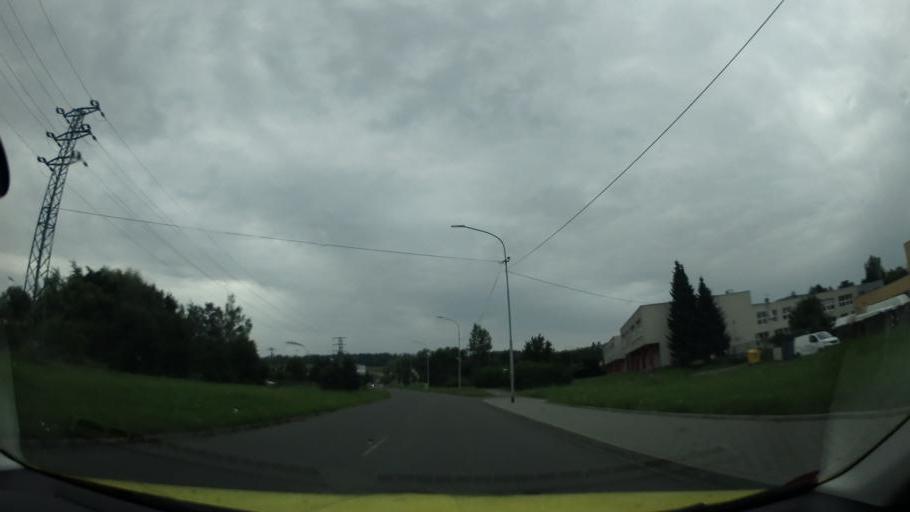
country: CZ
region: Moravskoslezsky
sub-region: Okres Novy Jicin
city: Novy Jicin
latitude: 49.5905
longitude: 17.9973
